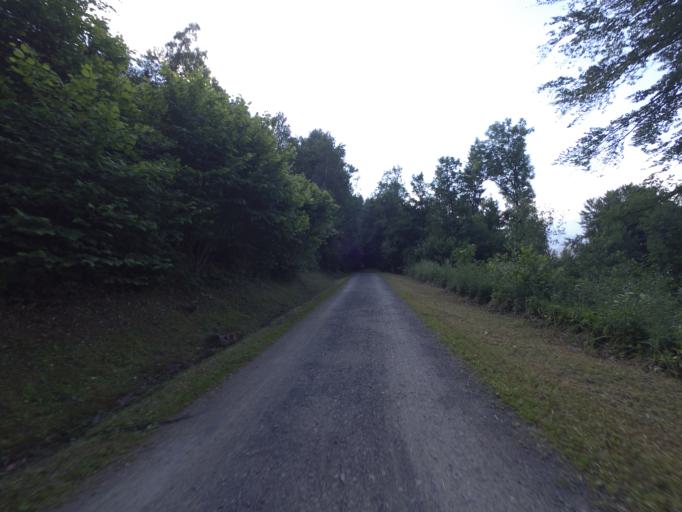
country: AT
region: Carinthia
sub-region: Politischer Bezirk Spittal an der Drau
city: Seeboden
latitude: 46.8024
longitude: 13.5447
